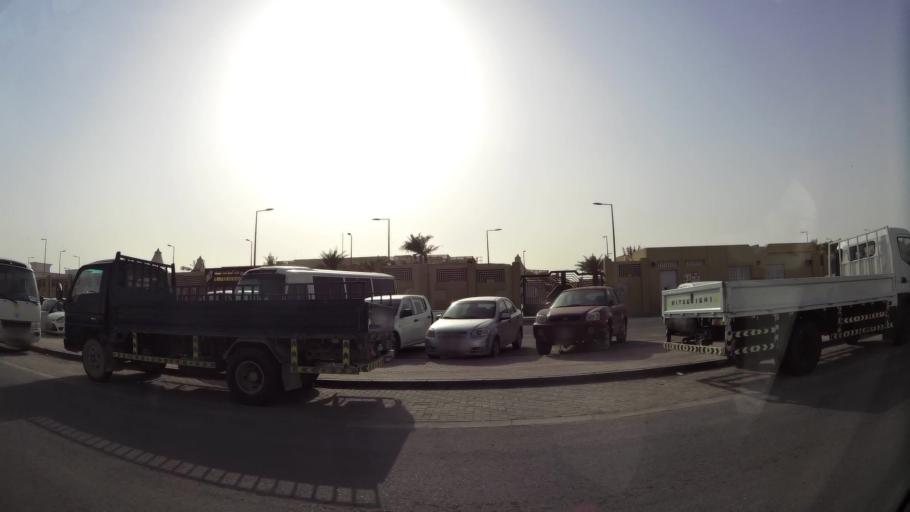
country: QA
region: Baladiyat ar Rayyan
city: Ar Rayyan
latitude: 25.2323
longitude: 51.4343
